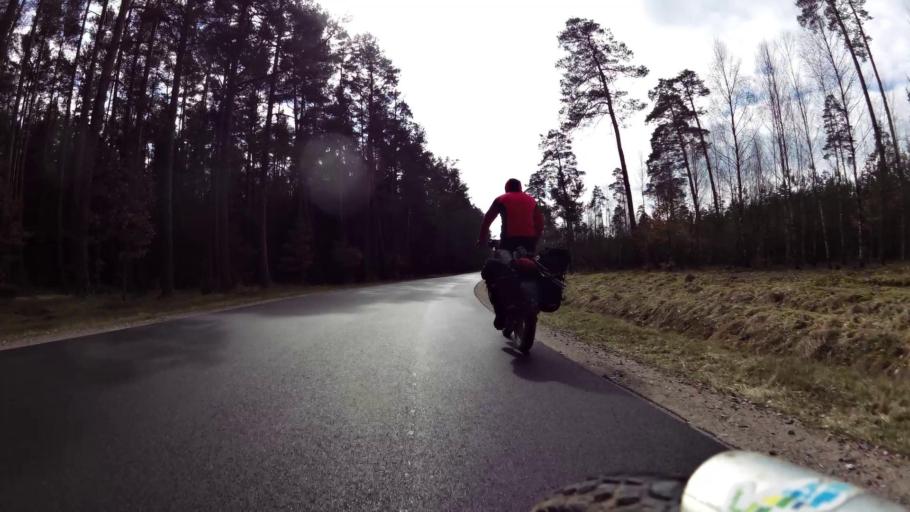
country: PL
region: Pomeranian Voivodeship
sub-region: Powiat bytowski
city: Kolczyglowy
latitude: 54.2027
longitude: 17.2353
